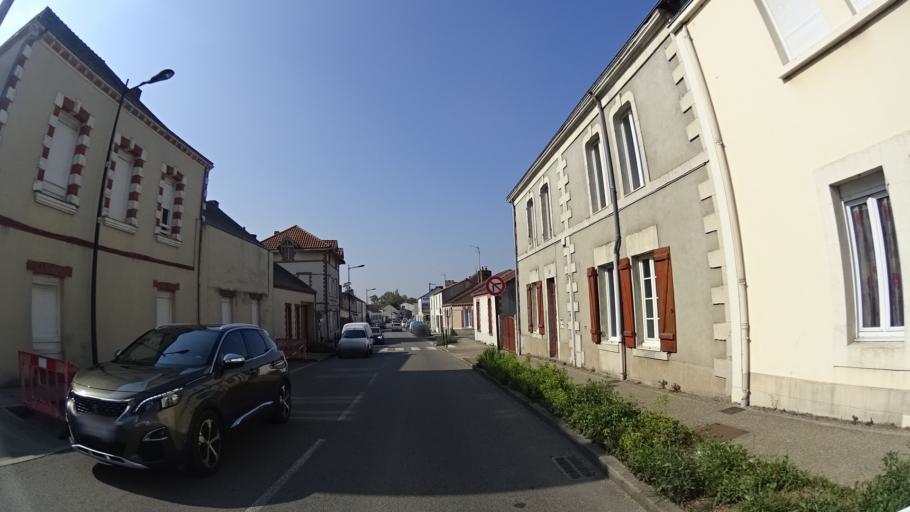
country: FR
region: Pays de la Loire
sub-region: Departement de la Loire-Atlantique
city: Sainte-Pazanne
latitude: 47.1023
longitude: -1.8118
